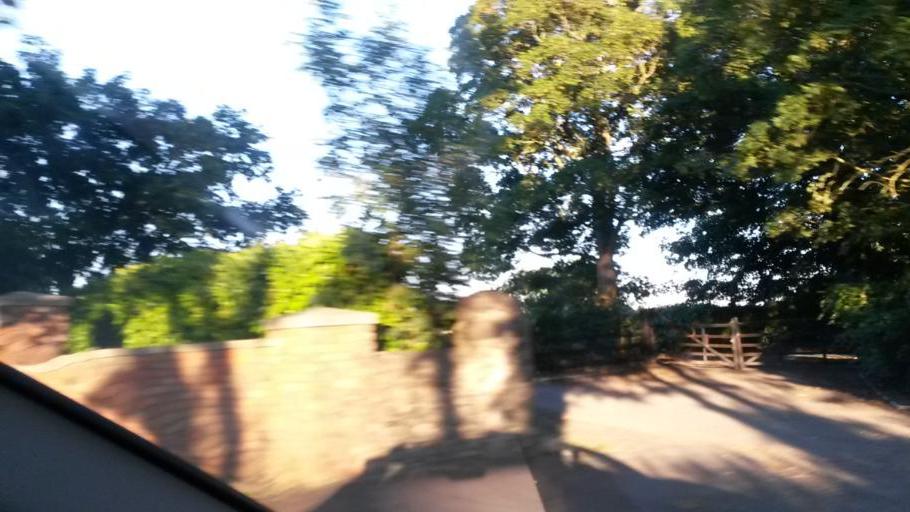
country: IE
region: Leinster
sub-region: An Mhi
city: Ashbourne
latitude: 53.4806
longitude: -6.3162
